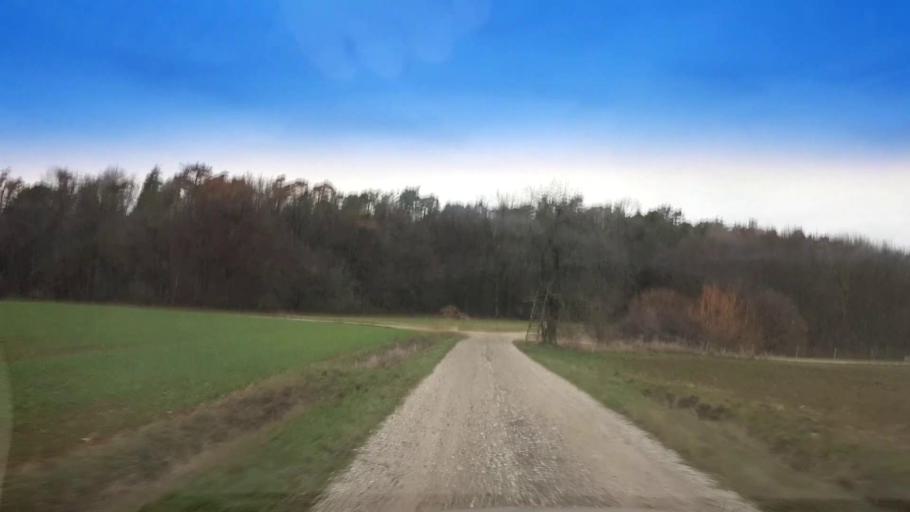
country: DE
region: Bavaria
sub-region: Upper Franconia
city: Hallerndorf
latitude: 49.7715
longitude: 10.9360
